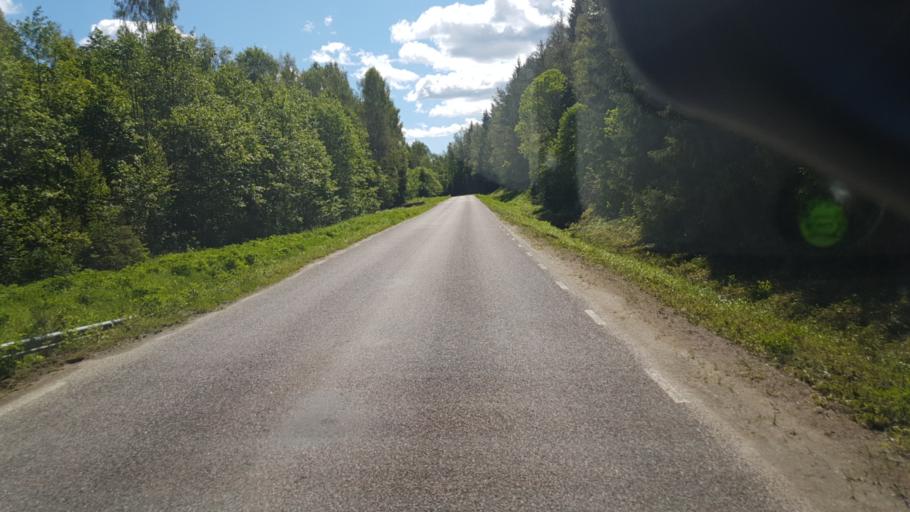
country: SE
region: Vaermland
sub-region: Grums Kommun
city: Grums
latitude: 59.5117
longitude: 12.8633
